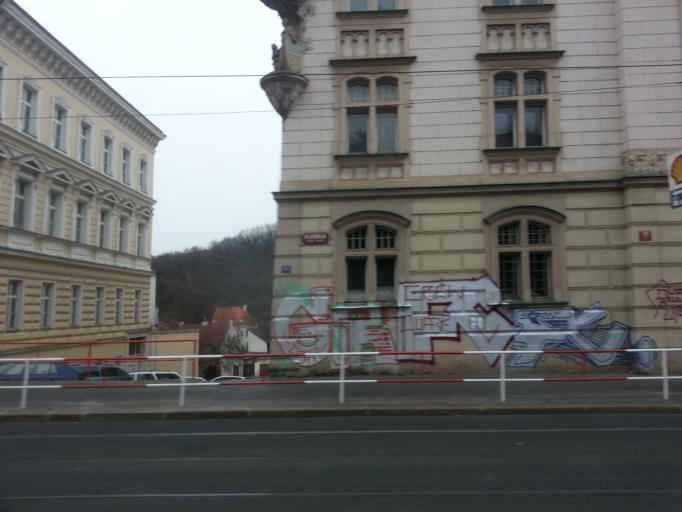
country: CZ
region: Praha
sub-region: Praha 1
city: Mala Strana
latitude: 50.0710
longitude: 14.3820
